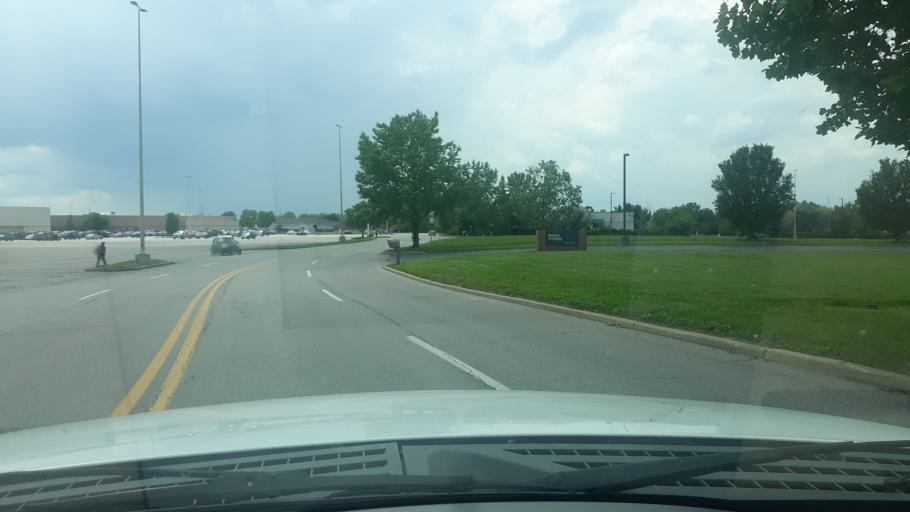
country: US
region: Illinois
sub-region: Williamson County
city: Marion
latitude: 37.7499
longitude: -88.9765
